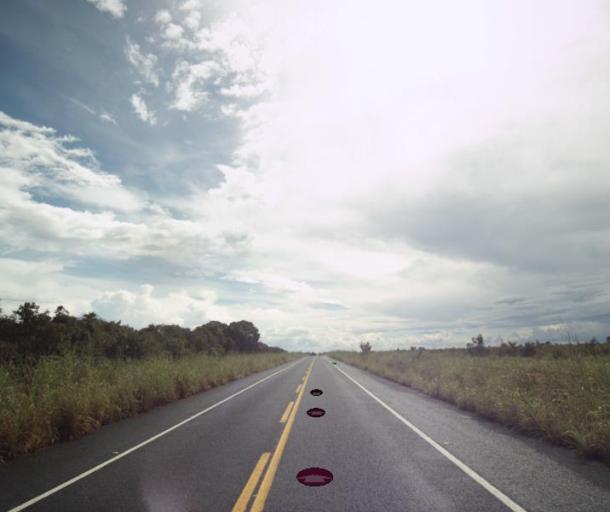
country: BR
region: Goias
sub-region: Sao Miguel Do Araguaia
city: Sao Miguel do Araguaia
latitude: -13.2924
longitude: -50.3995
